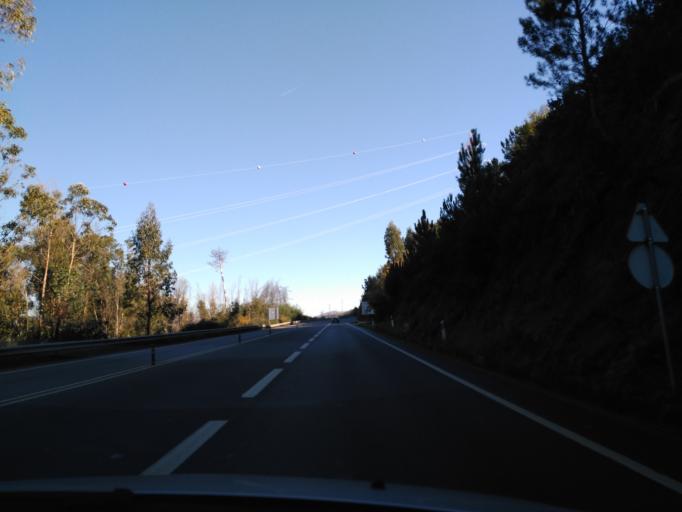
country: PT
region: Braga
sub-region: Braga
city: Adaufe
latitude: 41.5845
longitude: -8.3681
